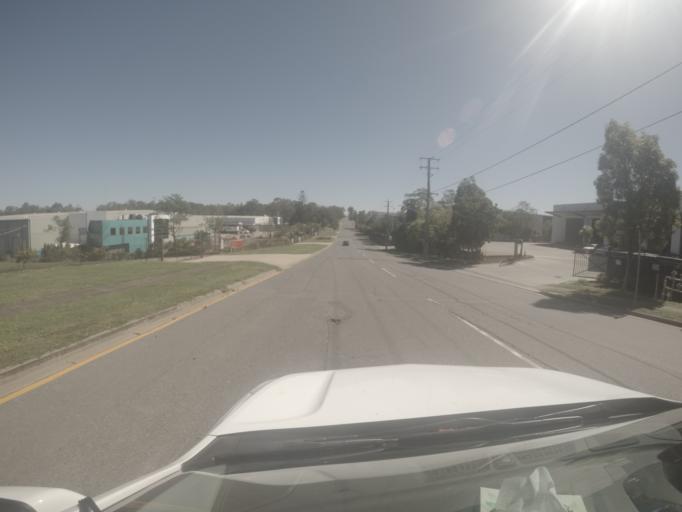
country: AU
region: Queensland
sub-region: Brisbane
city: Richlands
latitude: -27.5749
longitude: 152.9641
